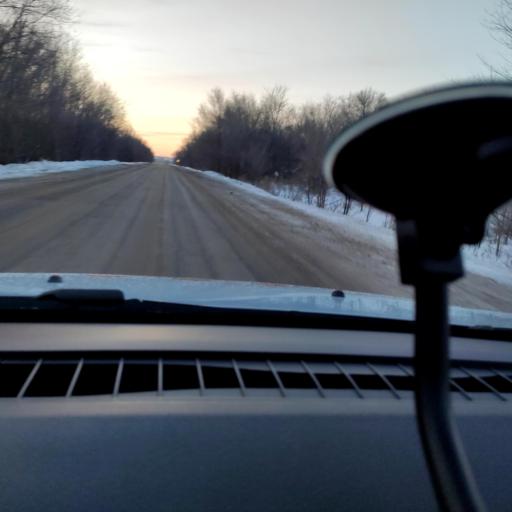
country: RU
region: Samara
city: Samara
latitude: 53.0972
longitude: 50.2295
